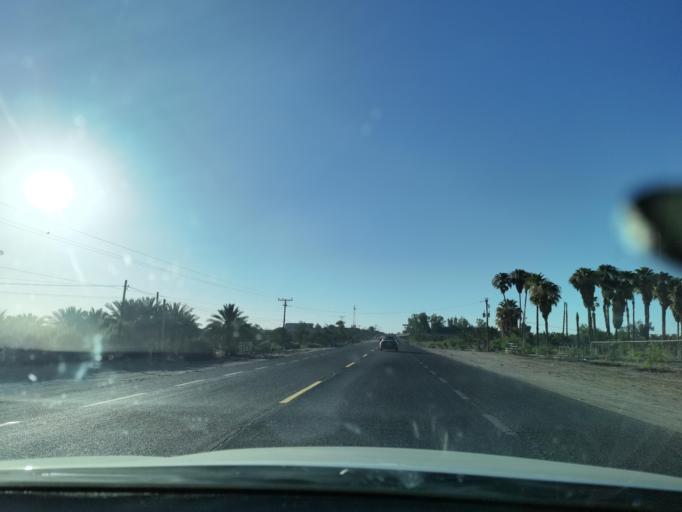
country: MX
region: Baja California
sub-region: Mexicali
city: Islas Agrarias Grupo A
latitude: 32.6421
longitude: -115.3064
